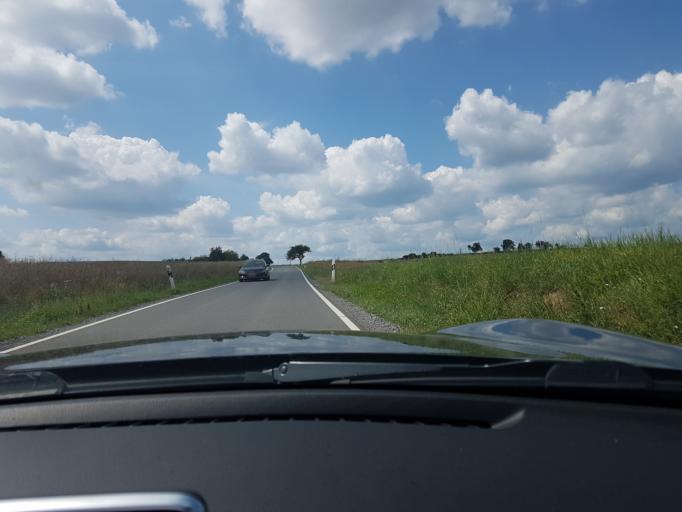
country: DE
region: Baden-Wuerttemberg
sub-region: Karlsruhe Region
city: Seckach
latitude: 49.4183
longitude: 9.2682
